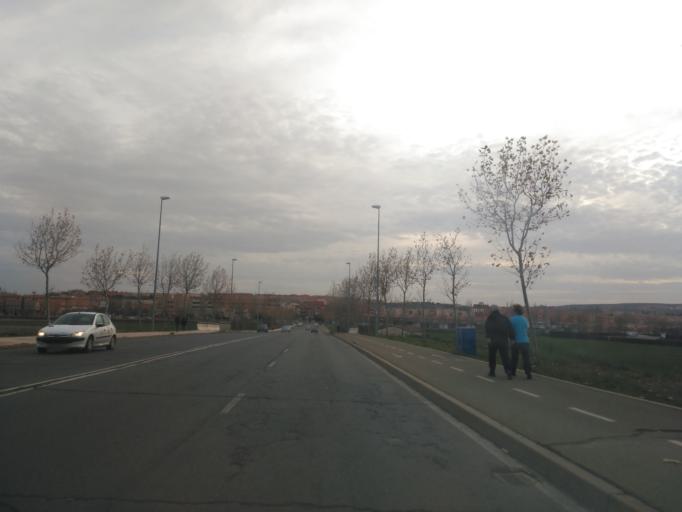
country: ES
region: Castille and Leon
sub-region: Provincia de Salamanca
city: Salamanca
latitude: 40.9614
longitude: -5.6812
